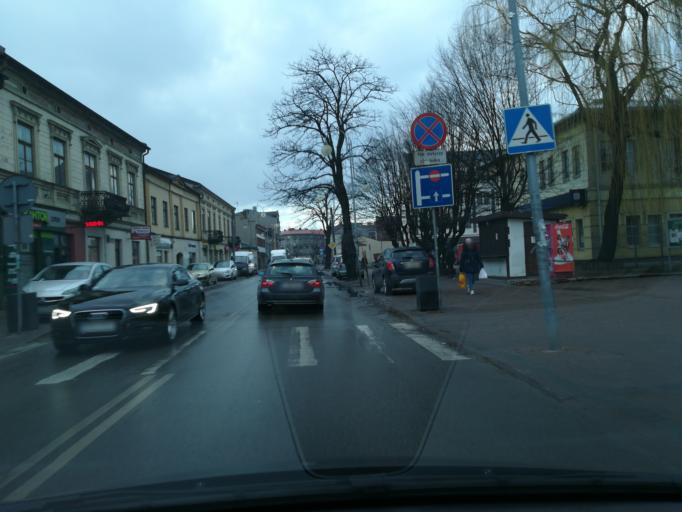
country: PL
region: Lodz Voivodeship
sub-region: Powiat radomszczanski
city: Radomsko
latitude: 51.0679
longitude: 19.4415
